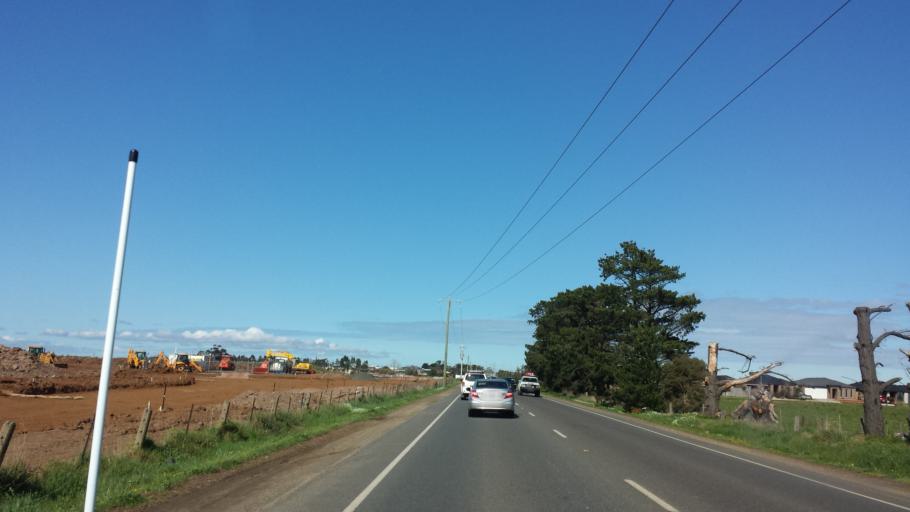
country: AU
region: Victoria
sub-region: Casey
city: Cranbourne East
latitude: -38.0967
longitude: 145.3314
